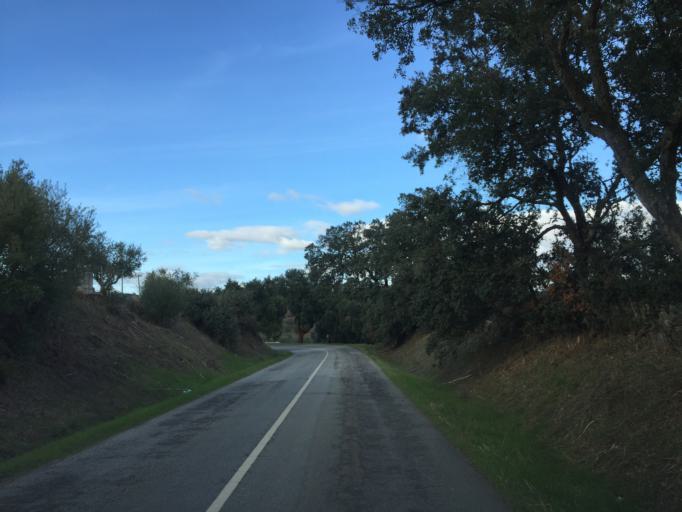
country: PT
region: Portalegre
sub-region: Alter do Chao
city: Alter do Chao
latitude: 39.2773
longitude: -7.6406
